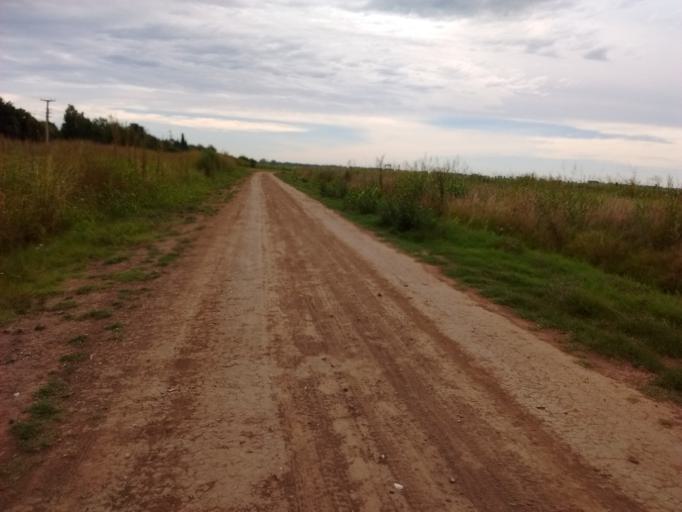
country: AR
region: Santa Fe
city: Funes
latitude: -32.9130
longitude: -60.8319
